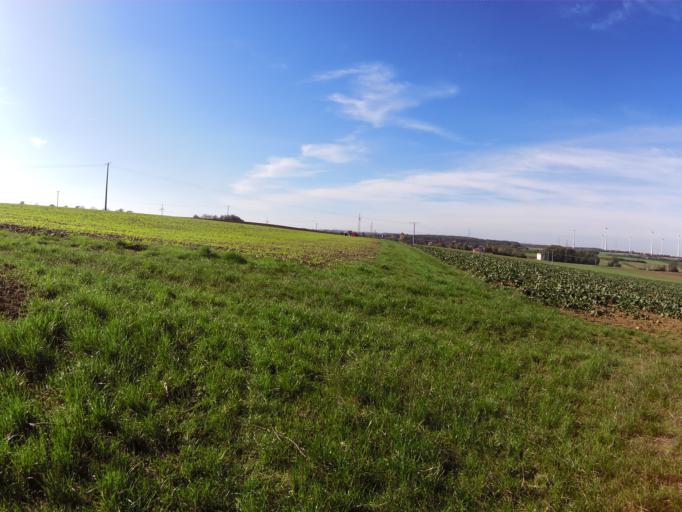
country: DE
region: Bavaria
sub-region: Regierungsbezirk Unterfranken
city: Sulzfeld am Main
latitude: 49.7089
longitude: 10.0946
